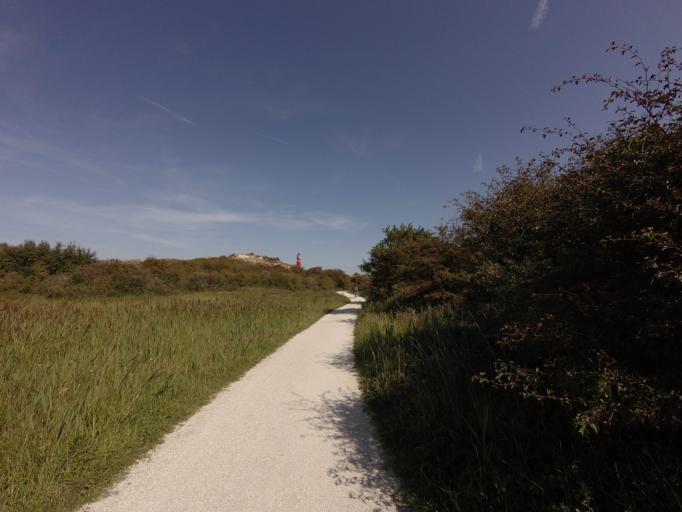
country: NL
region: Friesland
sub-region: Gemeente Schiermonnikoog
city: Schiermonnikoog
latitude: 53.4838
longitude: 6.1472
